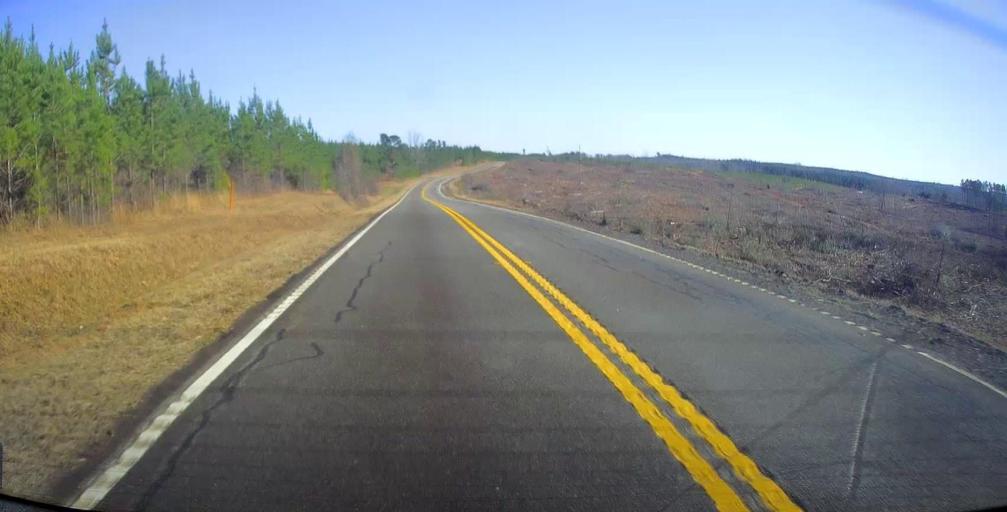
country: US
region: Georgia
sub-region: Talbot County
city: Talbotton
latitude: 32.6640
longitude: -84.4626
